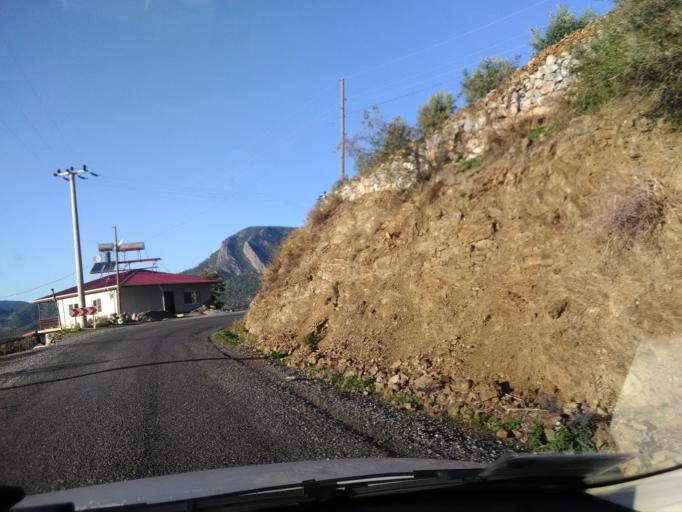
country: TR
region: Antalya
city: Gazipasa
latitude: 36.3087
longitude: 32.4069
